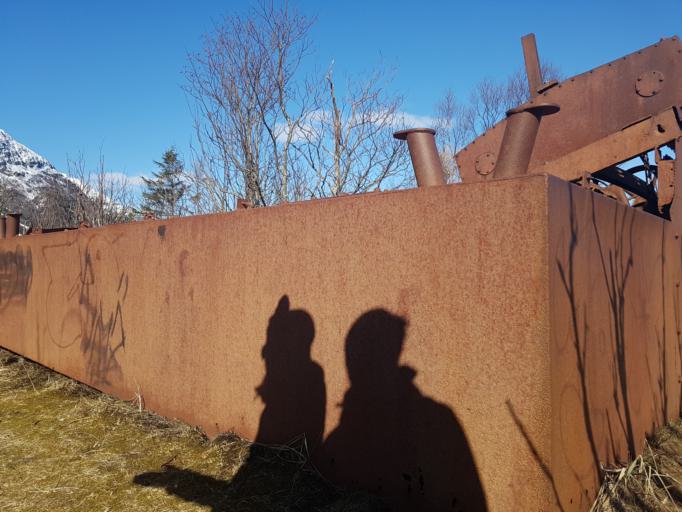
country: NO
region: Nordland
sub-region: Vefsn
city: Mosjoen
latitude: 65.8440
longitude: 13.1797
